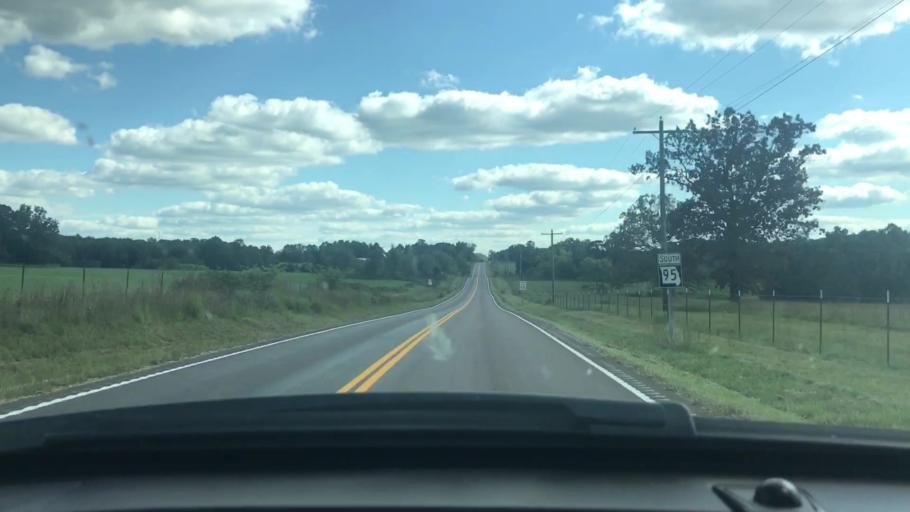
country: US
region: Missouri
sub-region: Wright County
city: Mountain Grove
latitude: 37.2422
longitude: -92.3004
